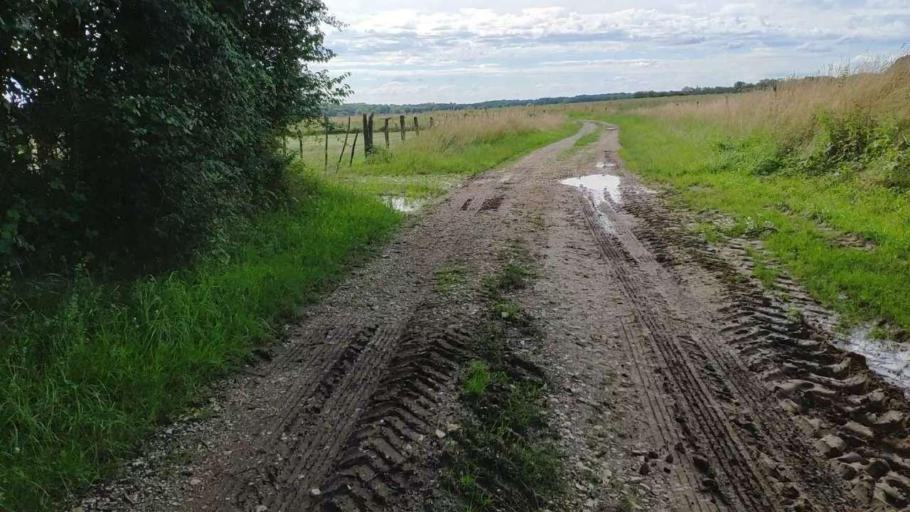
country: FR
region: Franche-Comte
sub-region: Departement du Jura
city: Bletterans
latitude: 46.8466
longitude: 5.5044
